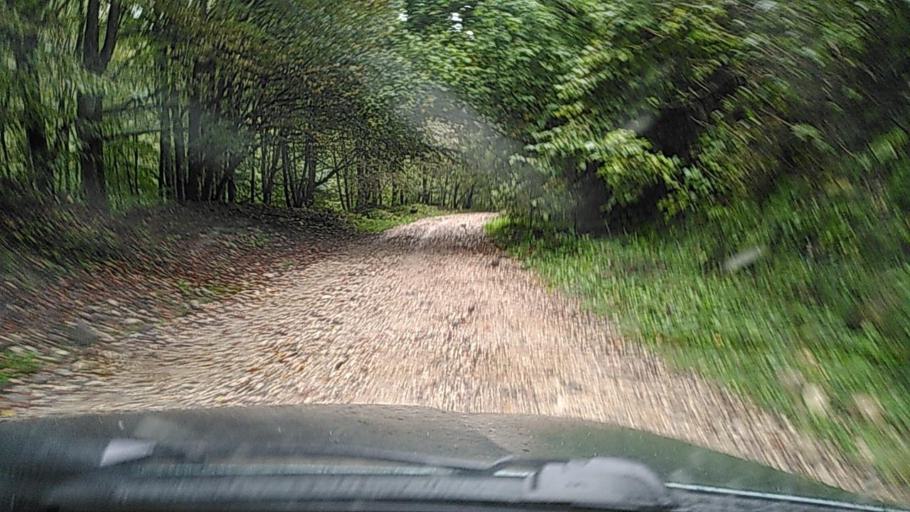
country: RU
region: Kabardino-Balkariya
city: Belaya Rechka
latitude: 43.3960
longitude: 43.4474
